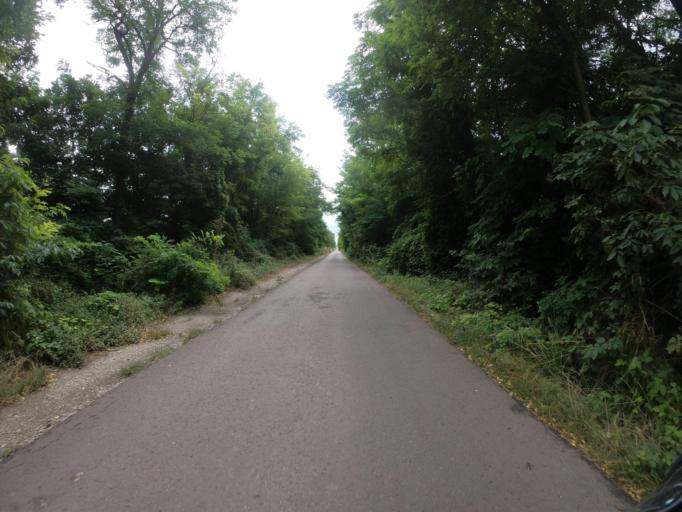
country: HU
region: Borsod-Abauj-Zemplen
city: Szentistvan
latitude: 47.7224
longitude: 20.6868
